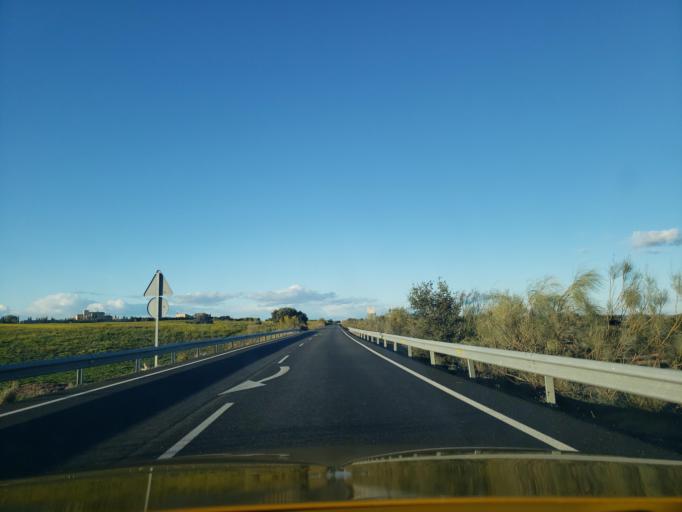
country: ES
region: Castille-La Mancha
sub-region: Province of Toledo
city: Cobisa
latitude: 39.8305
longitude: -4.0185
